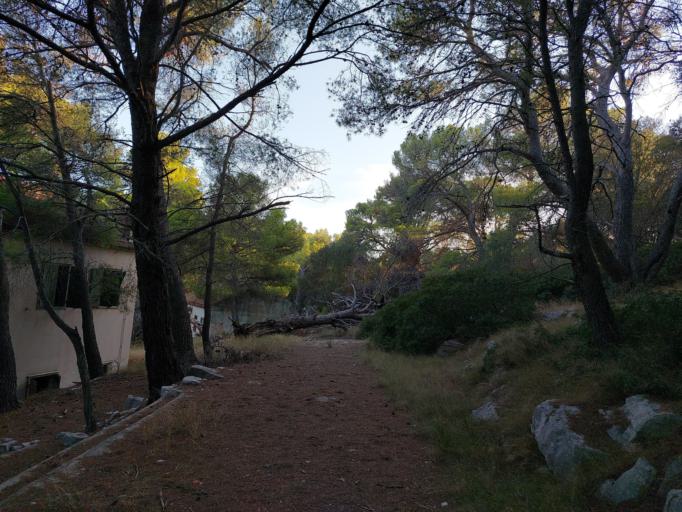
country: HR
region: Dubrovacko-Neretvanska
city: Smokvica
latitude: 42.7708
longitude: 16.7905
